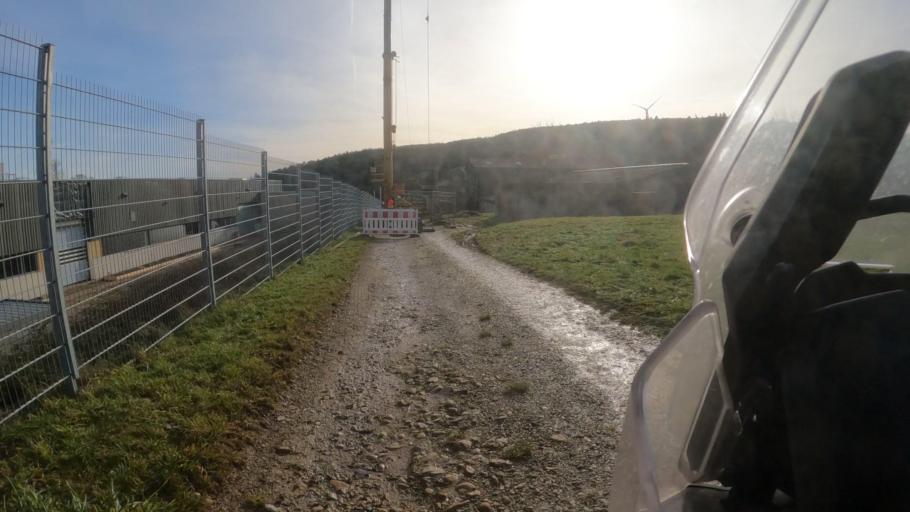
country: DE
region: Baden-Wuerttemberg
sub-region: Freiburg Region
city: Tengen
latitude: 47.7855
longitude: 8.6301
